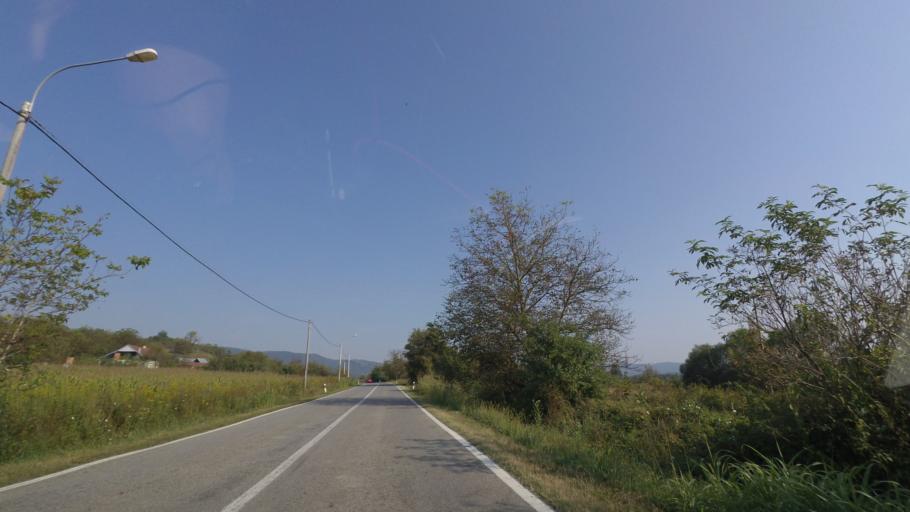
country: HR
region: Brodsko-Posavska
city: Resetari
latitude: 45.3862
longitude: 17.5099
